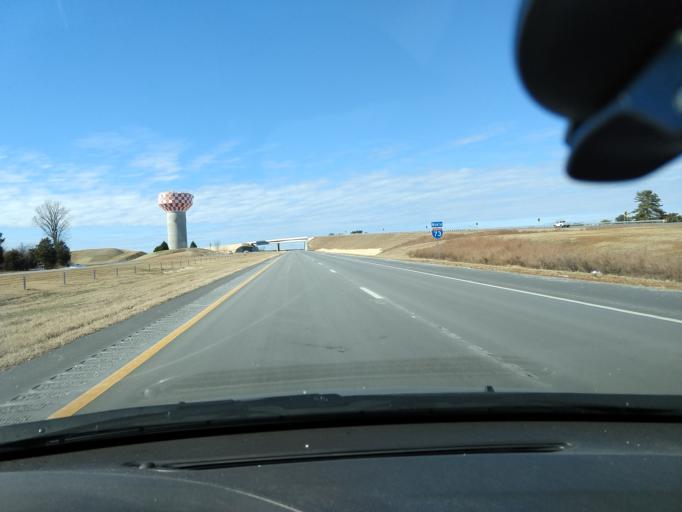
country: US
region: North Carolina
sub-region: Guilford County
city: Oak Ridge
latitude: 36.1216
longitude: -79.9553
